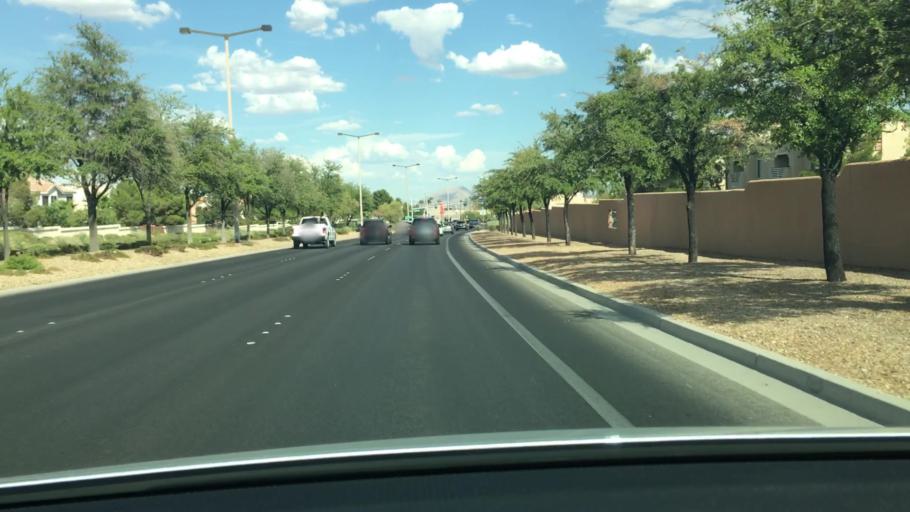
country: US
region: Nevada
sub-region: Clark County
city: Spring Valley
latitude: 36.1971
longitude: -115.2679
